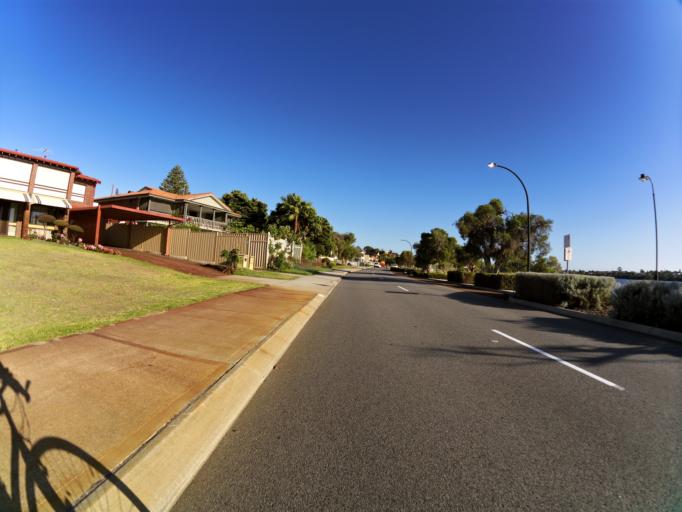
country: AU
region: Western Australia
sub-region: Melville
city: Mount Pleasant
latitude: -32.0285
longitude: 115.8525
